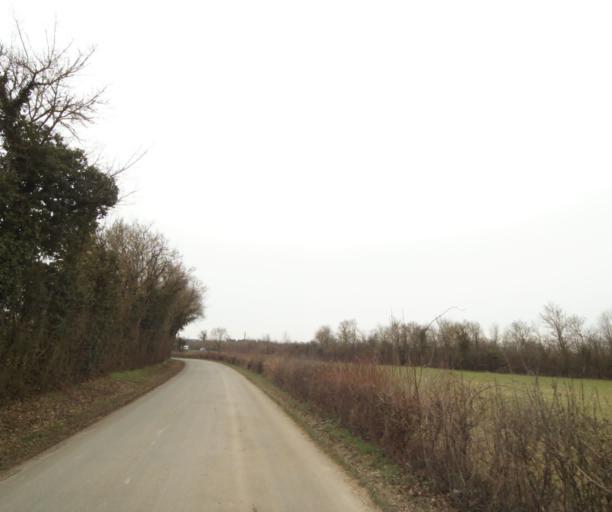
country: FR
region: Poitou-Charentes
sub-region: Departement des Deux-Sevres
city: Magne
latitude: 46.3298
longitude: -0.5288
